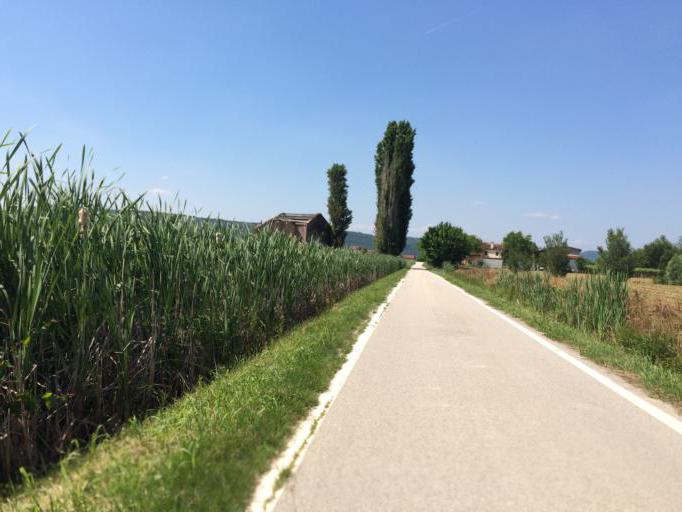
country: IT
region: Veneto
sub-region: Provincia di Vicenza
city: Sossano
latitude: 45.3449
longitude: 11.4942
